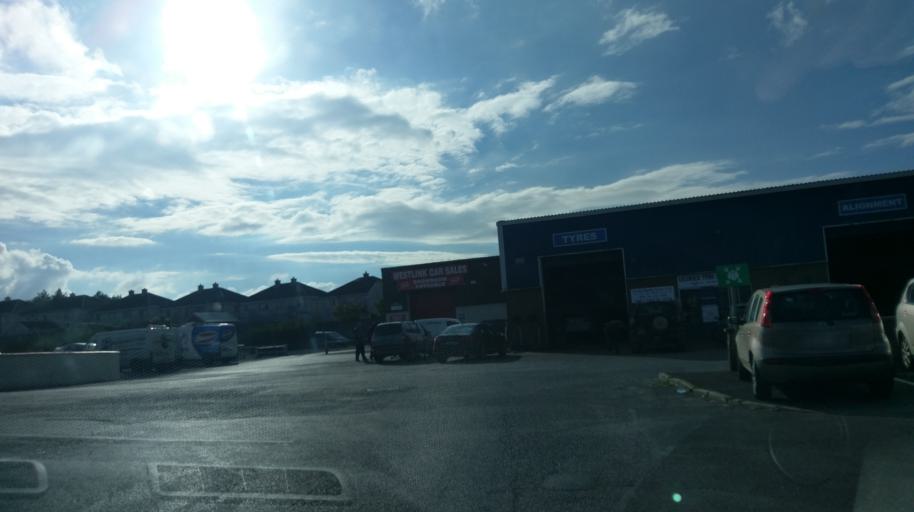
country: IE
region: Connaught
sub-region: County Galway
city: Gaillimh
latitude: 53.2895
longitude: -9.0256
